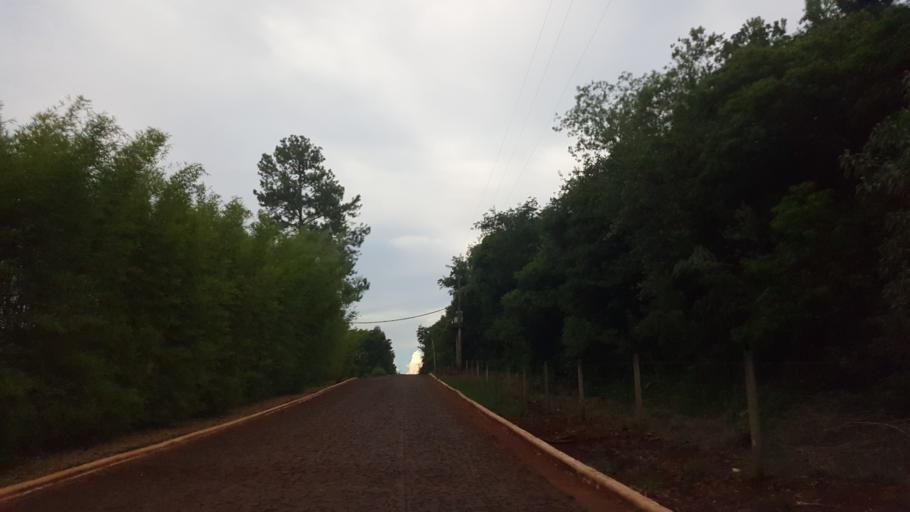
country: AR
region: Misiones
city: Jardin America
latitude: -27.0797
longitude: -55.2864
